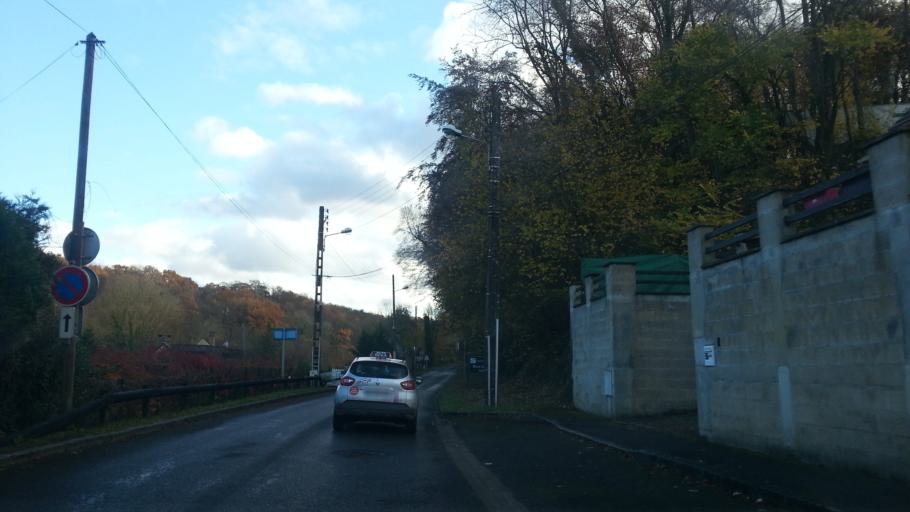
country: FR
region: Picardie
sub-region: Departement de l'Oise
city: Verneuil-en-Halatte
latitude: 49.2649
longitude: 2.5350
